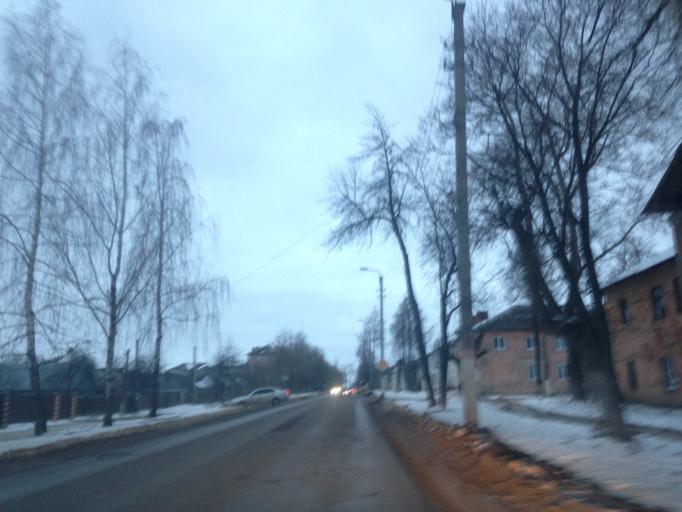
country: RU
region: Tula
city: Shchekino
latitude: 54.0015
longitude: 37.5270
